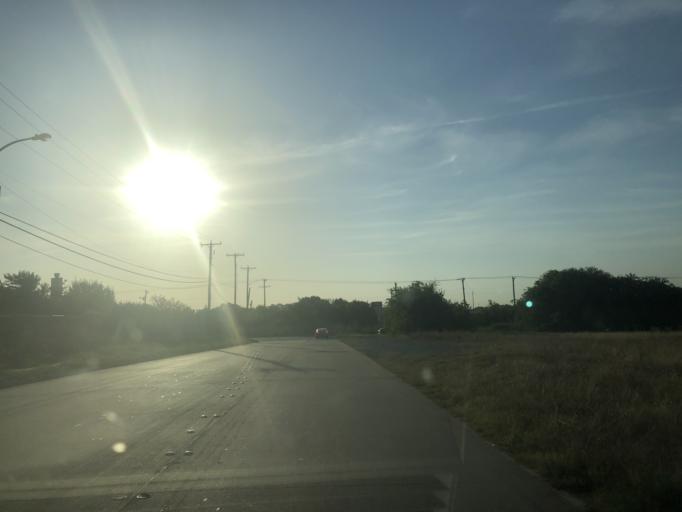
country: US
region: Texas
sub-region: Tarrant County
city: White Settlement
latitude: 32.7317
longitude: -97.5049
